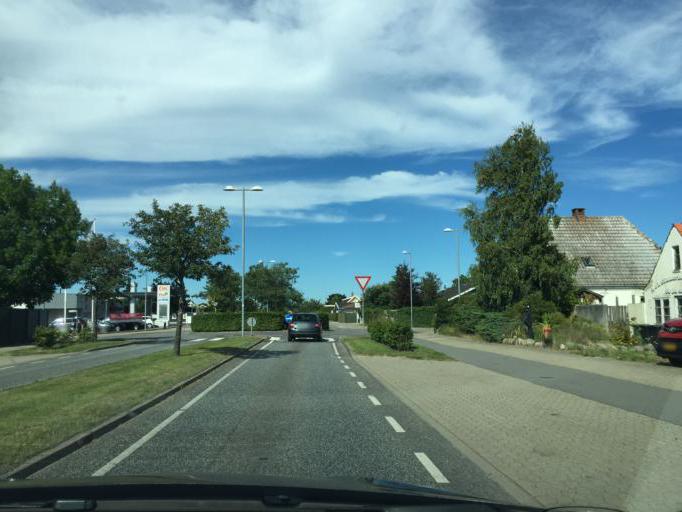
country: DK
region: Zealand
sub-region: Solrod Kommune
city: Solrod Strand
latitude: 55.5248
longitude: 12.2165
